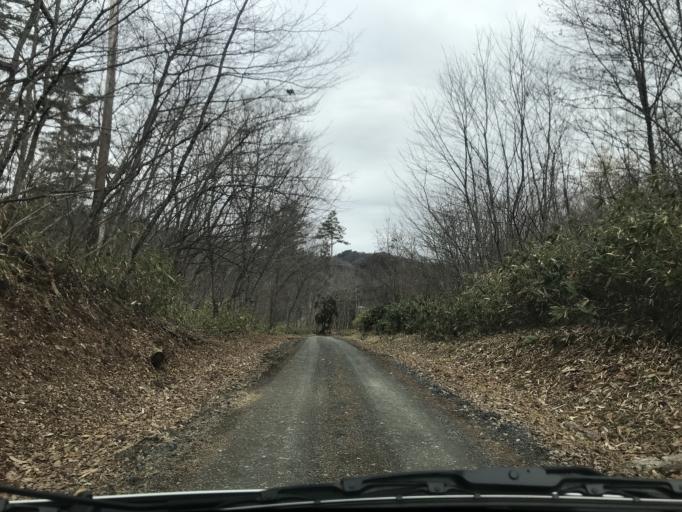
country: JP
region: Iwate
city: Kitakami
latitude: 39.3208
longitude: 141.2275
